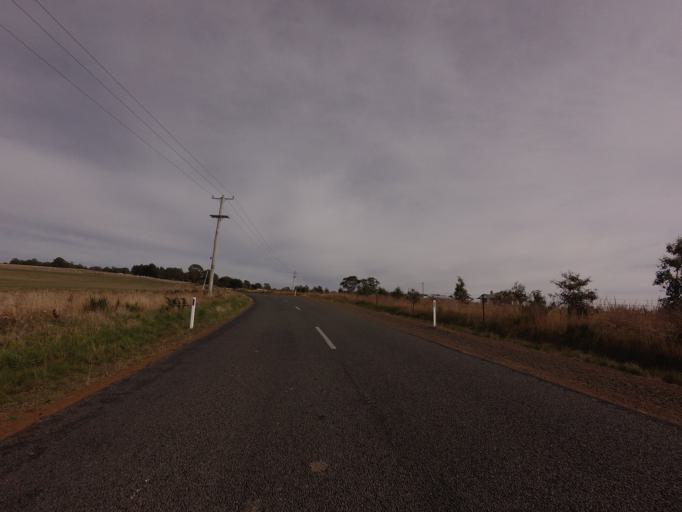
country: AU
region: Tasmania
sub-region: Brighton
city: Bridgewater
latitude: -42.3905
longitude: 147.4287
